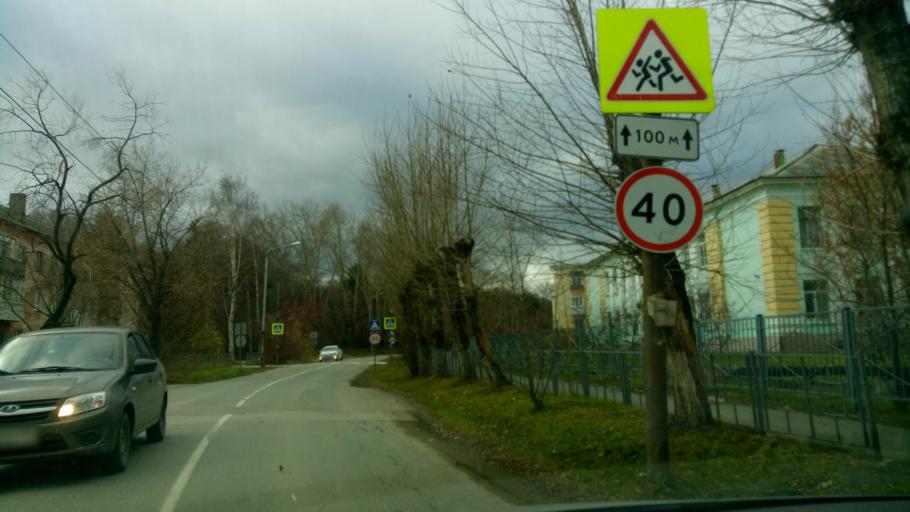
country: RU
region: Sverdlovsk
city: Sredneuralsk
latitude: 56.9900
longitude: 60.4715
